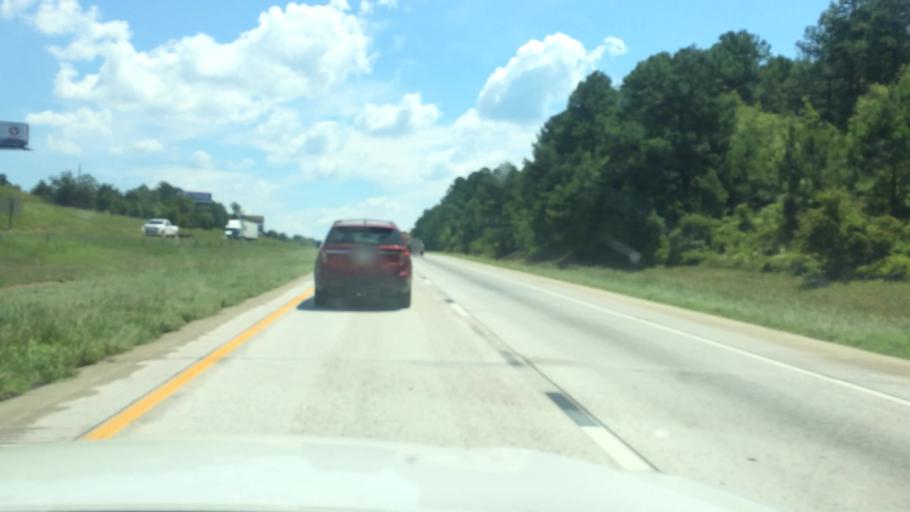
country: US
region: South Carolina
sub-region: Aiken County
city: Belvedere
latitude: 33.5466
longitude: -81.9652
